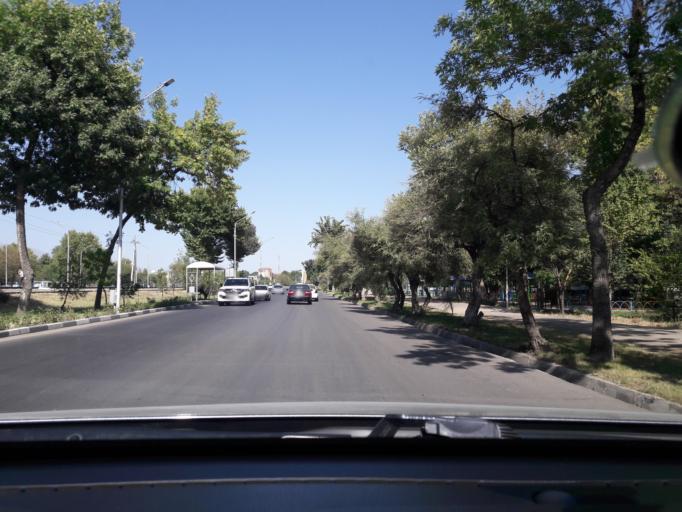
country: TJ
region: Dushanbe
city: Dushanbe
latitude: 38.5688
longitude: 68.7522
